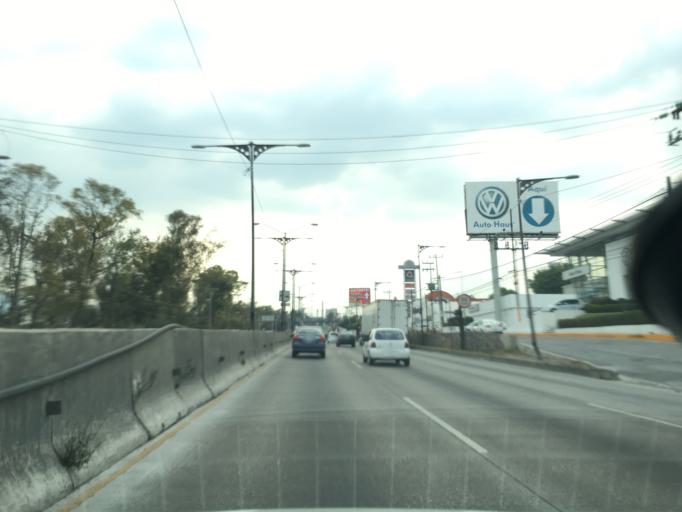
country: MX
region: Mexico City
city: Col. Bosques de las Lomas
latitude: 19.3833
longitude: -99.2512
